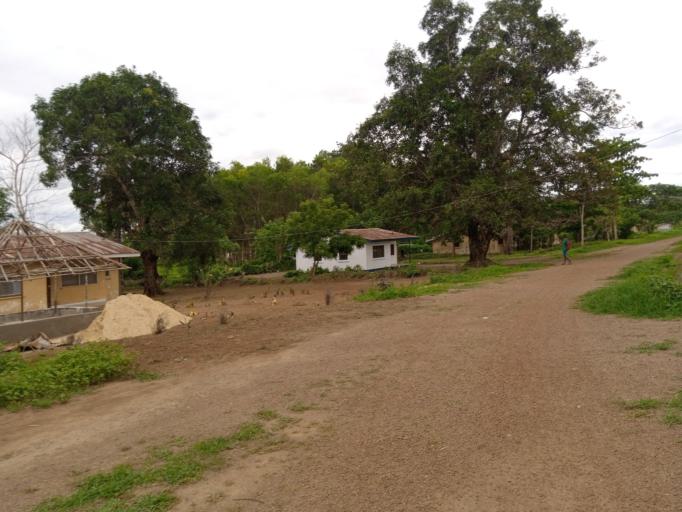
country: SL
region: Southern Province
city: Largo
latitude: 8.1125
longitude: -12.0683
